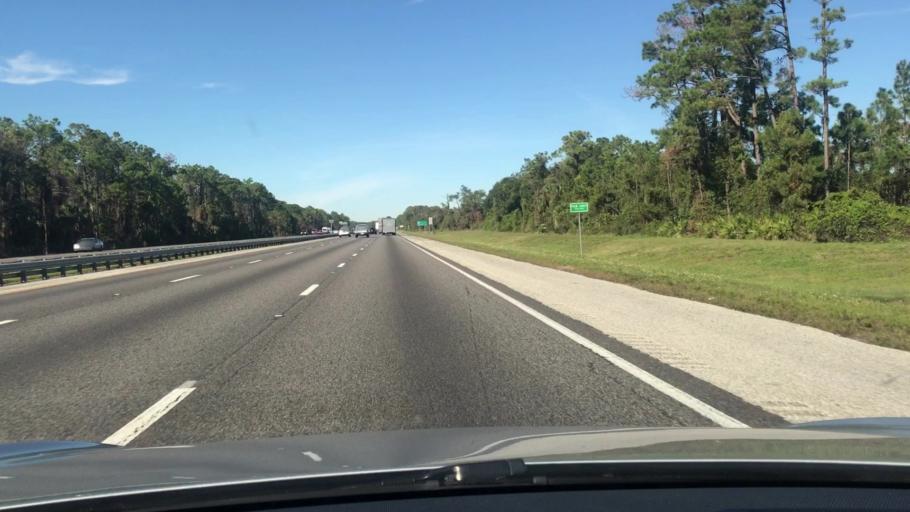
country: US
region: Florida
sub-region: Flagler County
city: Flagler Beach
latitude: 29.4147
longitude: -81.1597
